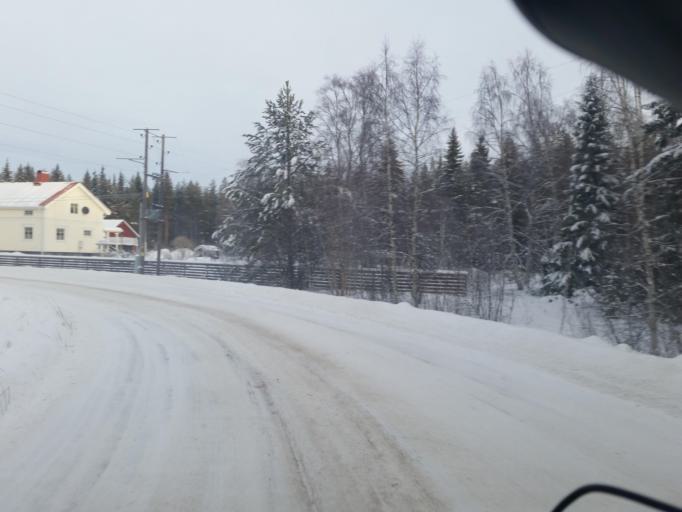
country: SE
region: Norrbotten
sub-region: Pitea Kommun
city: Rosvik
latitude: 65.4065
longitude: 21.7585
